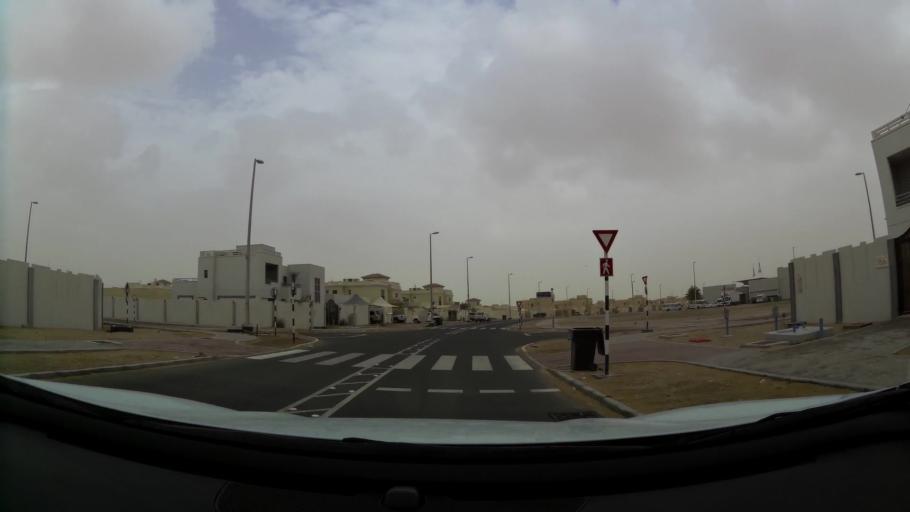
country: AE
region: Abu Dhabi
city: Abu Dhabi
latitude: 24.4447
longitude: 54.7160
